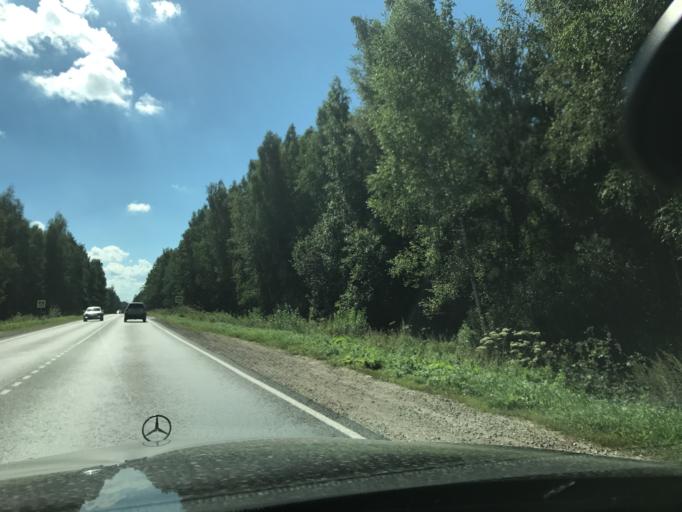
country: RU
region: Vladimir
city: Vorsha
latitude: 56.0906
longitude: 40.0951
